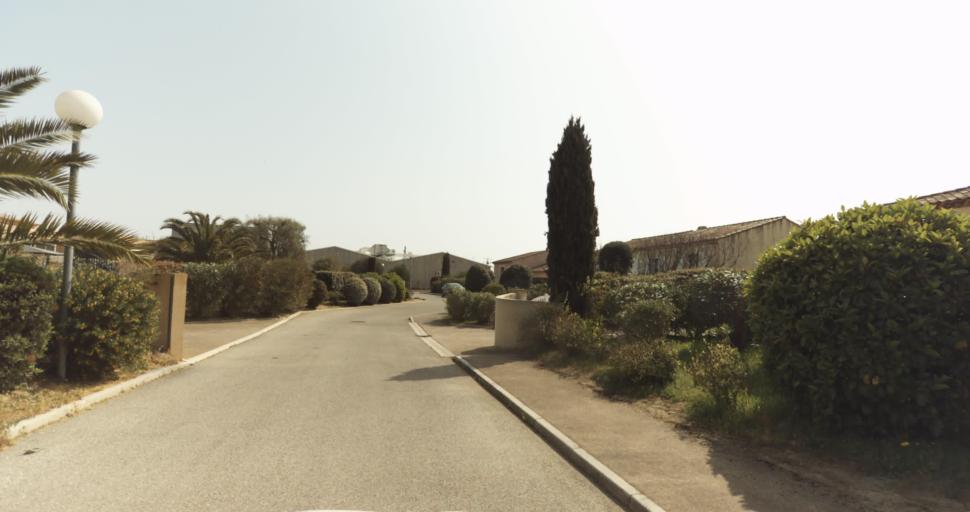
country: FR
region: Provence-Alpes-Cote d'Azur
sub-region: Departement du Var
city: Bormes-les-Mimosas
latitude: 43.1340
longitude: 6.3456
